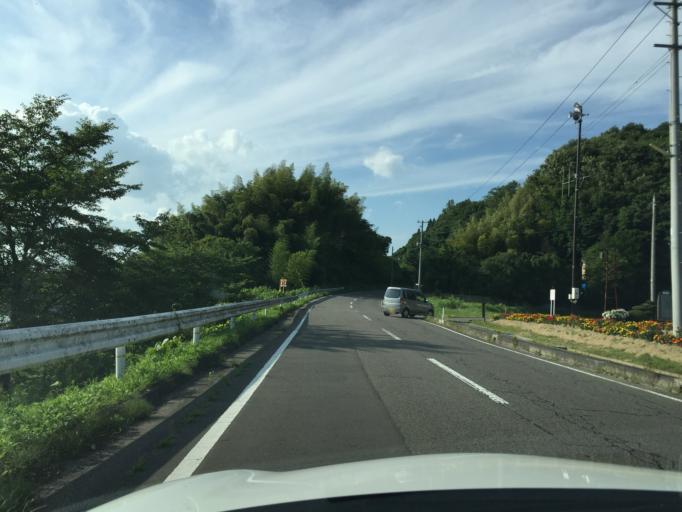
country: JP
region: Fukushima
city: Miharu
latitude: 37.3935
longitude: 140.5039
